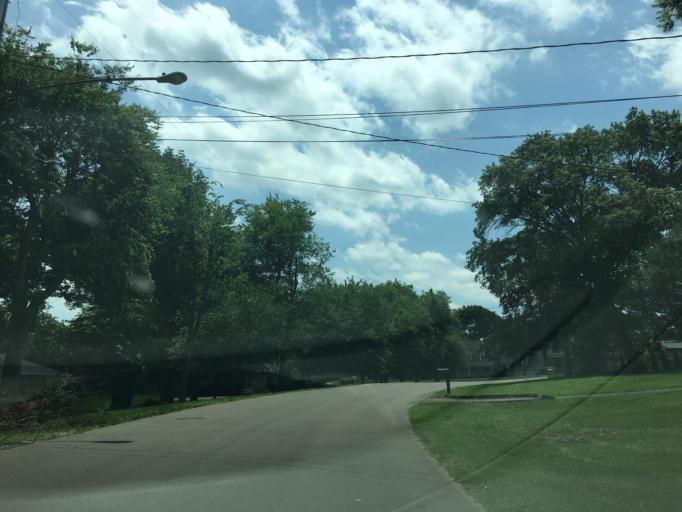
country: US
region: Tennessee
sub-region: Davidson County
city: Belle Meade
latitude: 36.1051
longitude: -86.8240
